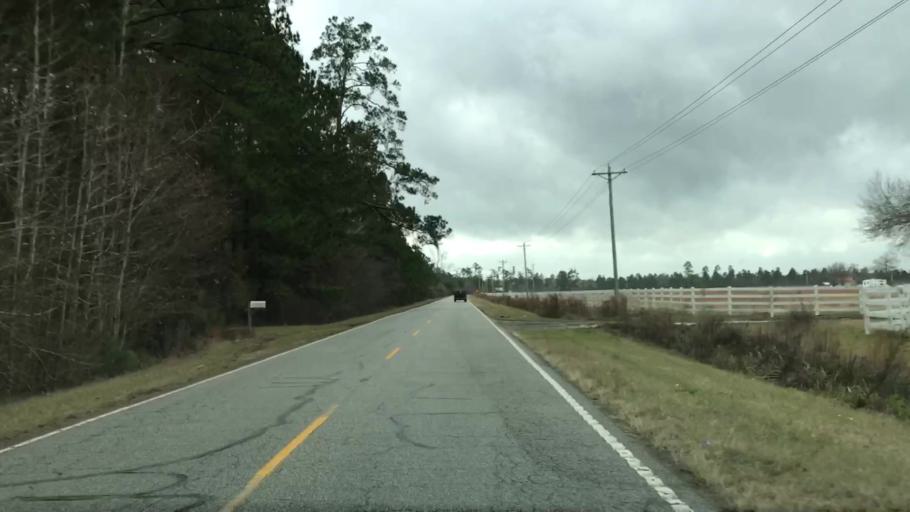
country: US
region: South Carolina
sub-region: Florence County
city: Johnsonville
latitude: 33.6548
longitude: -79.4193
